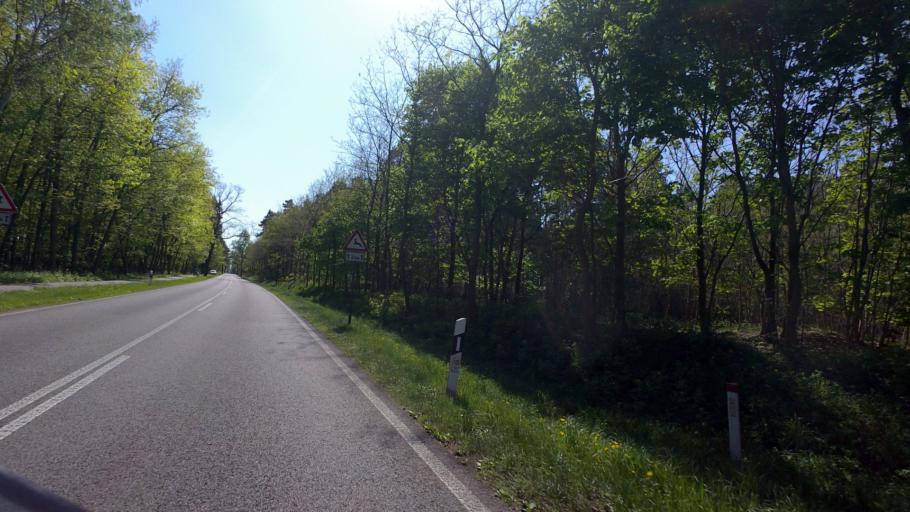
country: DE
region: Brandenburg
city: Tauche
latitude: 52.1368
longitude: 14.2034
